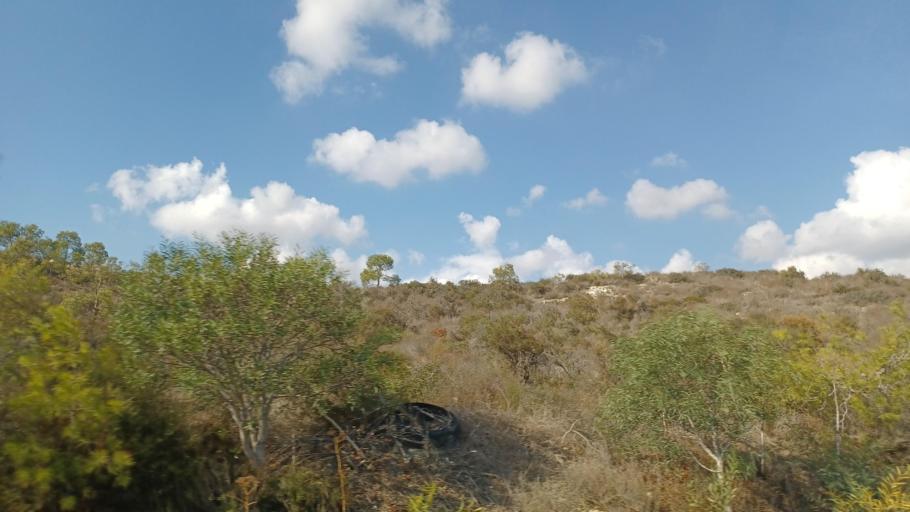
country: CY
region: Limassol
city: Pyrgos
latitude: 34.7259
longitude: 33.2755
